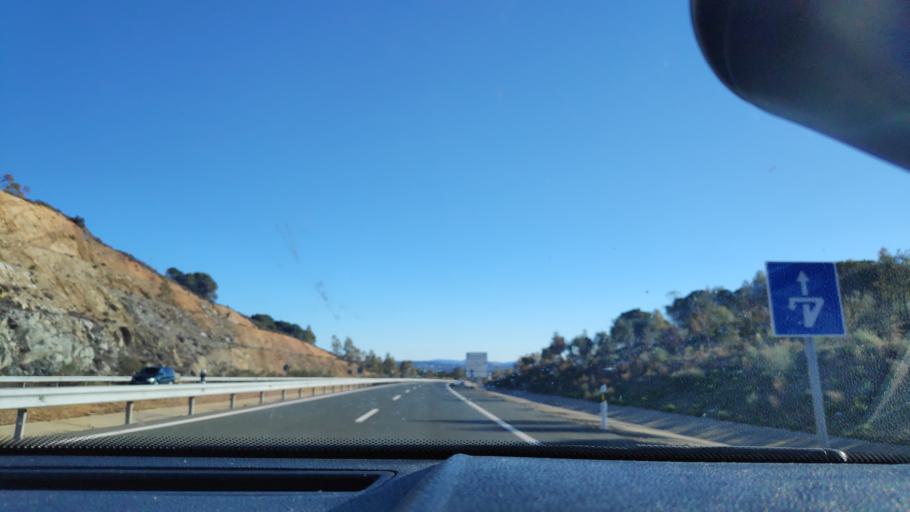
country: ES
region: Extremadura
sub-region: Provincia de Badajoz
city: Monesterio
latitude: 38.0388
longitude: -6.2265
